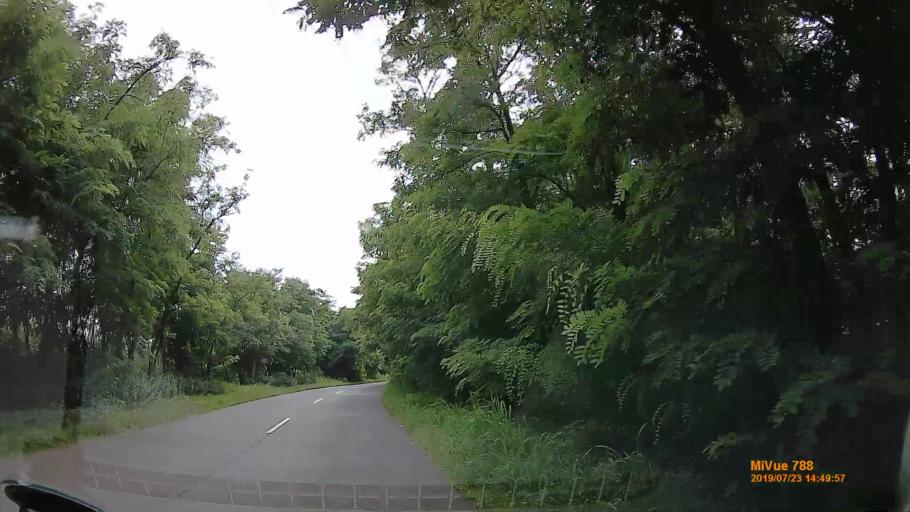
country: HU
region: Szabolcs-Szatmar-Bereg
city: Kalmanhaza
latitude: 47.8919
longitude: 21.6594
